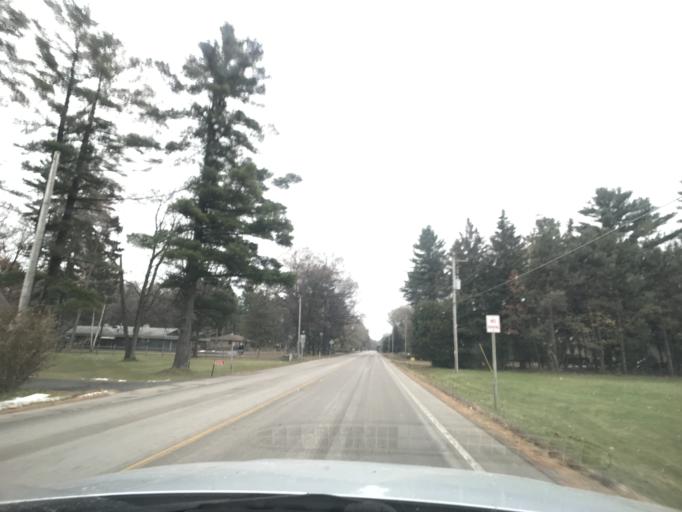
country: US
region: Wisconsin
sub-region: Marinette County
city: Marinette
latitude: 45.0695
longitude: -87.6194
